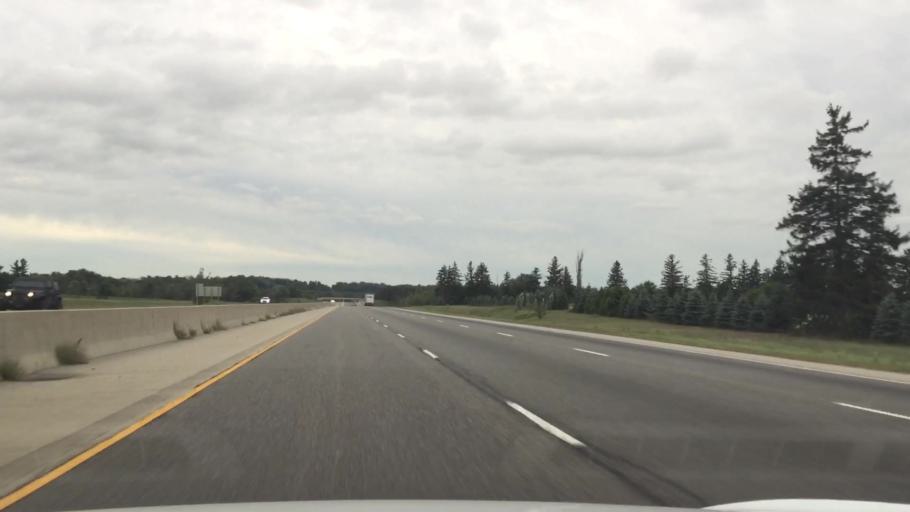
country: CA
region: Ontario
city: Kitchener
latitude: 43.3102
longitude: -80.4761
